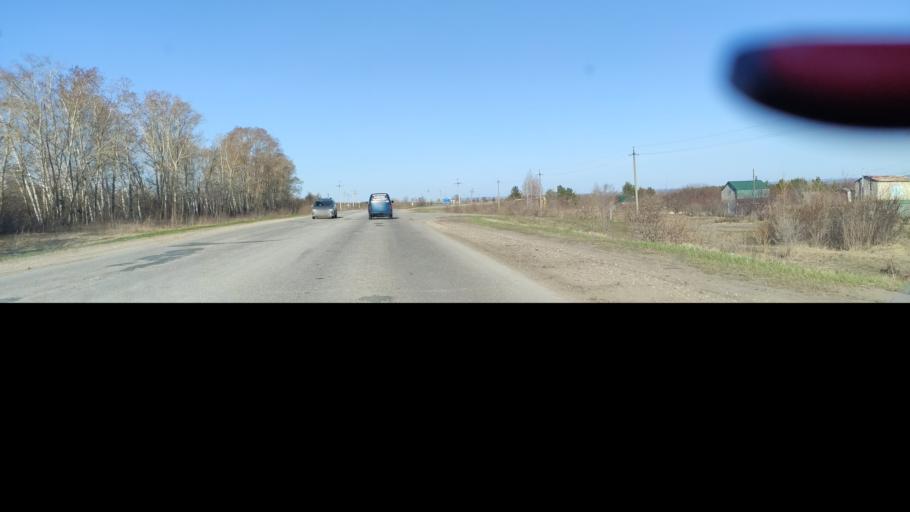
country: RU
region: Samara
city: Varlamovo
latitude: 53.1230
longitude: 48.3016
